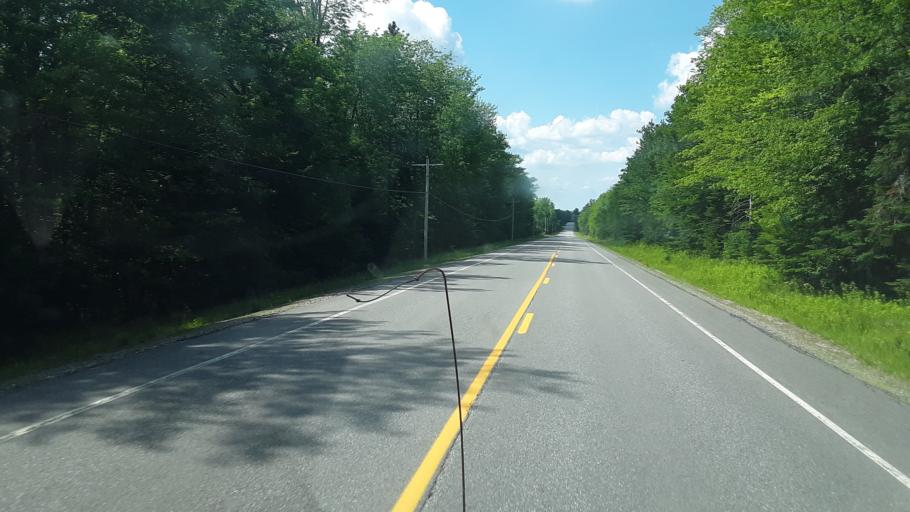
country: US
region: Maine
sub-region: Washington County
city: Machias
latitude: 45.0132
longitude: -67.5552
